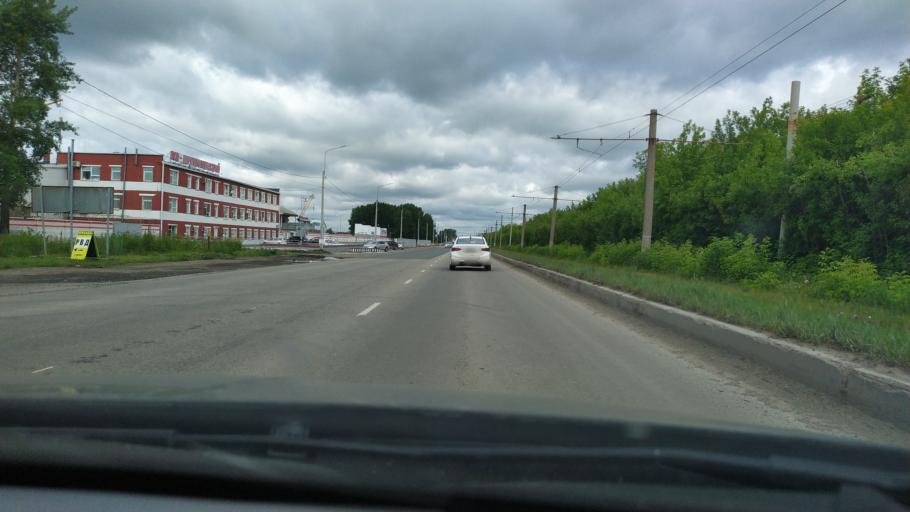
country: RU
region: Perm
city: Kondratovo
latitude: 57.9266
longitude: 56.1350
